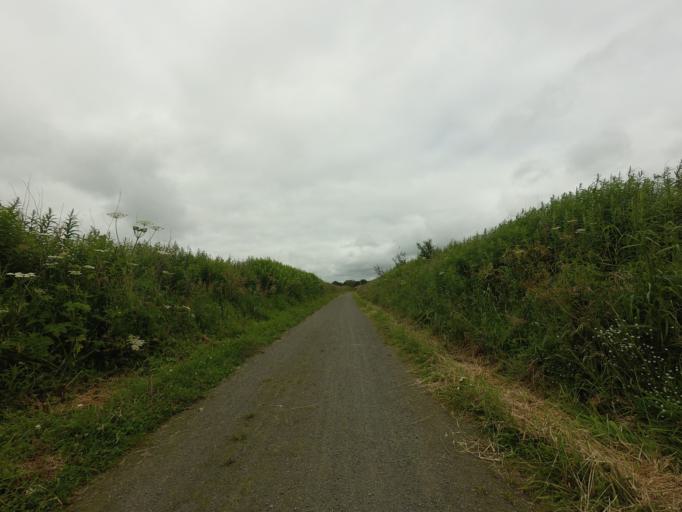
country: GB
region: Scotland
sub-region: Aberdeenshire
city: Ellon
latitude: 57.4842
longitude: -2.1350
